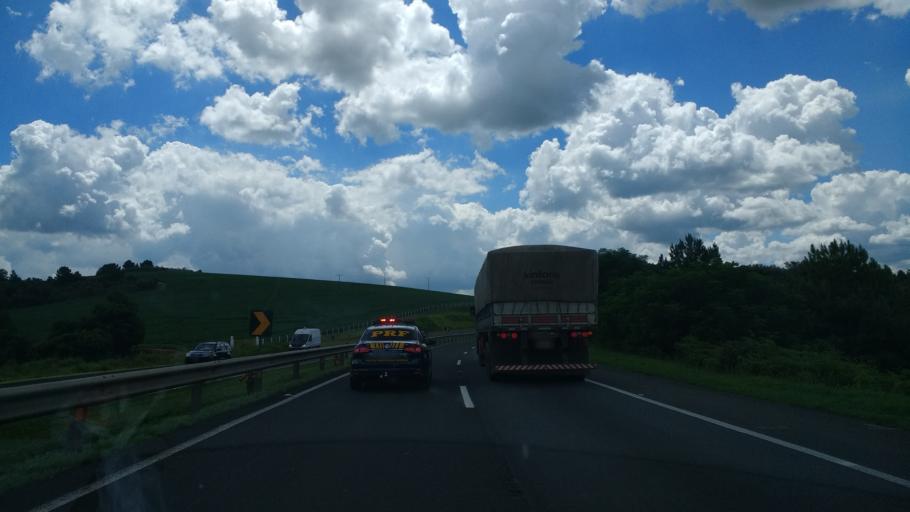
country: BR
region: Parana
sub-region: Palmeira
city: Palmeira
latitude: -25.2666
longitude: -49.9697
